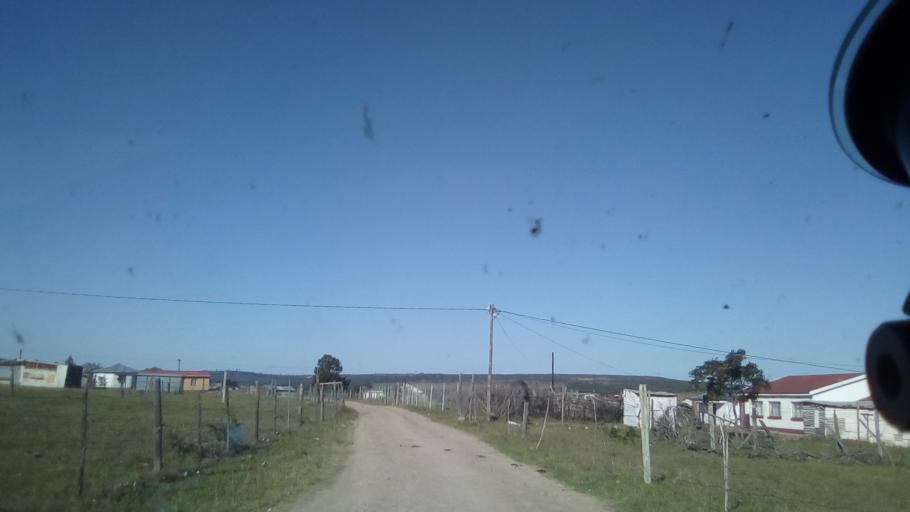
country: ZA
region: Eastern Cape
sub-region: Buffalo City Metropolitan Municipality
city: Bhisho
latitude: -32.8274
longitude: 27.3704
